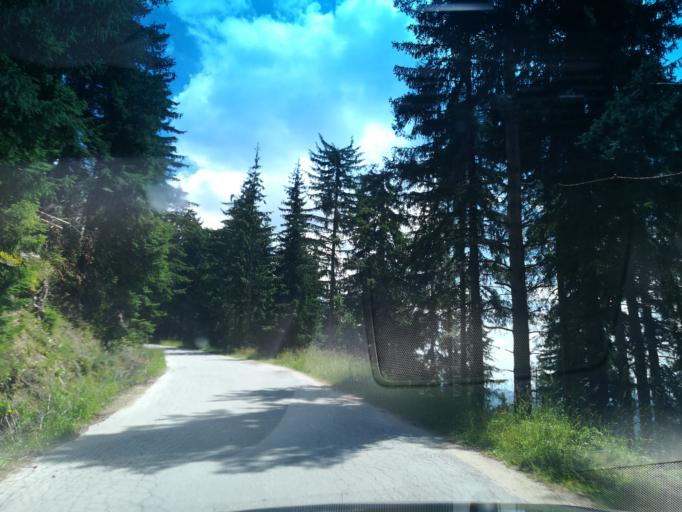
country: BG
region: Smolyan
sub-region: Obshtina Chepelare
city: Chepelare
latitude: 41.6928
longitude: 24.7771
